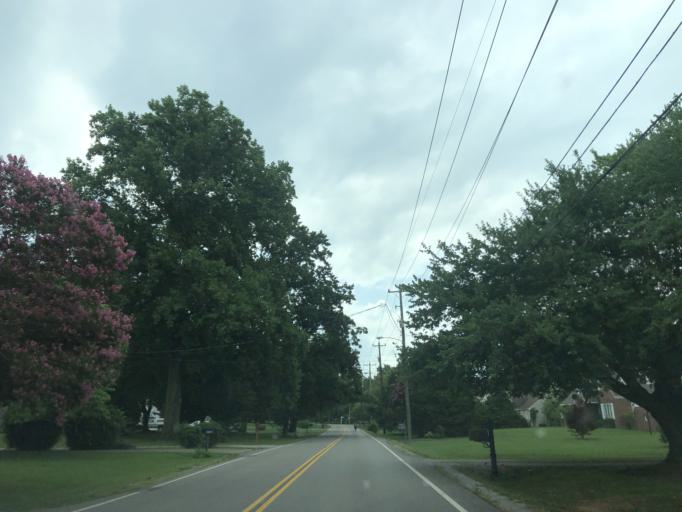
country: US
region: Tennessee
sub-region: Davidson County
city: Lakewood
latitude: 36.1665
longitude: -86.6679
